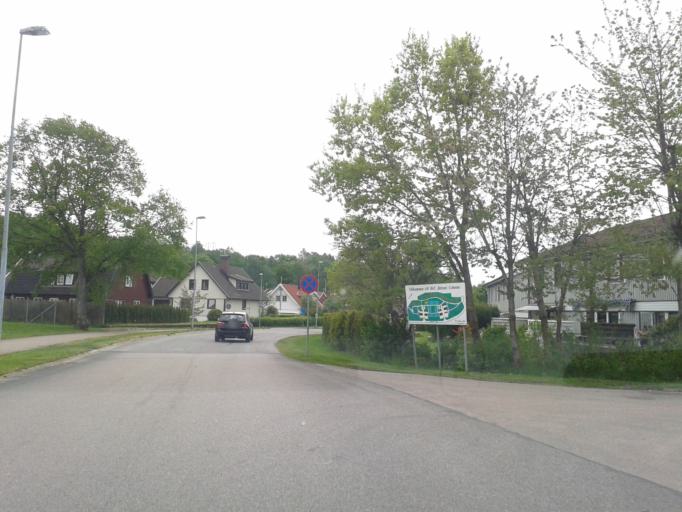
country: SE
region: Vaestra Goetaland
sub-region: Kungalvs Kommun
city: Kungalv
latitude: 57.8846
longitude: 11.9636
